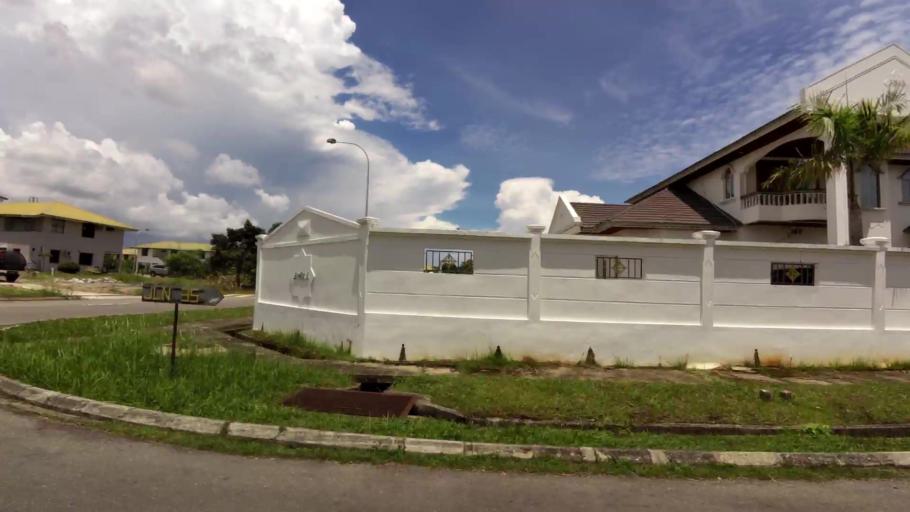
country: BN
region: Brunei and Muara
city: Bandar Seri Begawan
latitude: 4.9619
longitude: 114.9156
